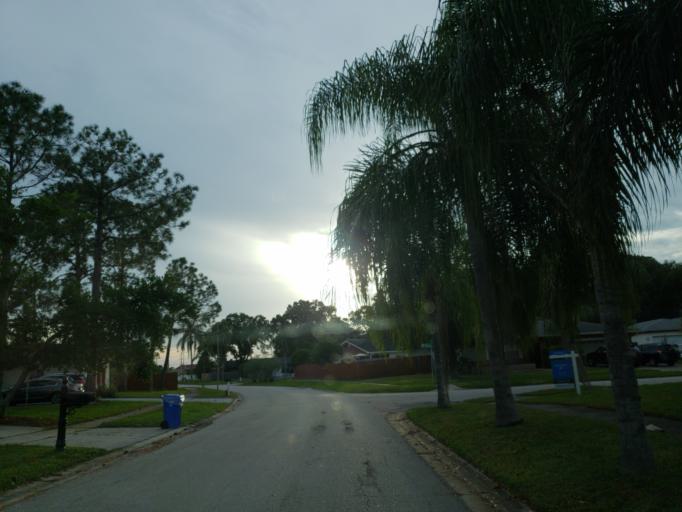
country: US
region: Florida
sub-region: Hillsborough County
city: Carrollwood Village
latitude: 28.0535
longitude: -82.5217
